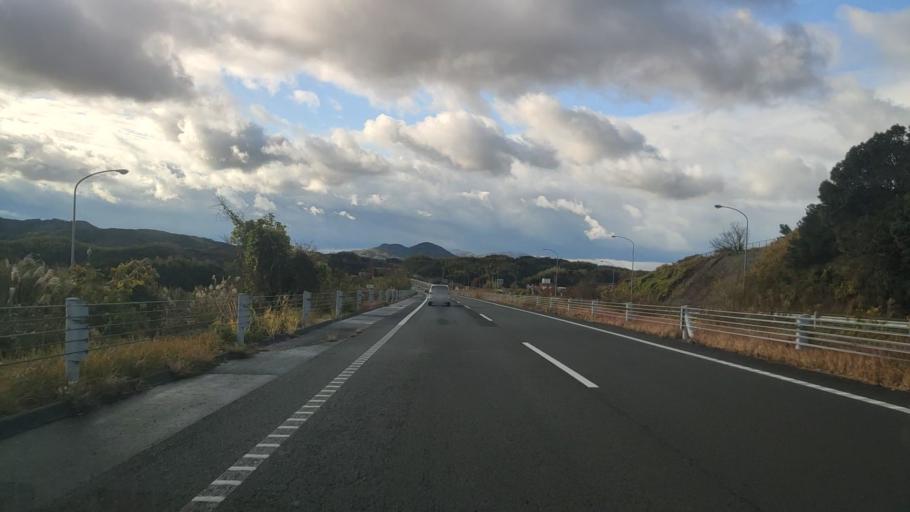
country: JP
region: Hyogo
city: Sumoto
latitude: 34.4448
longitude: 134.8746
